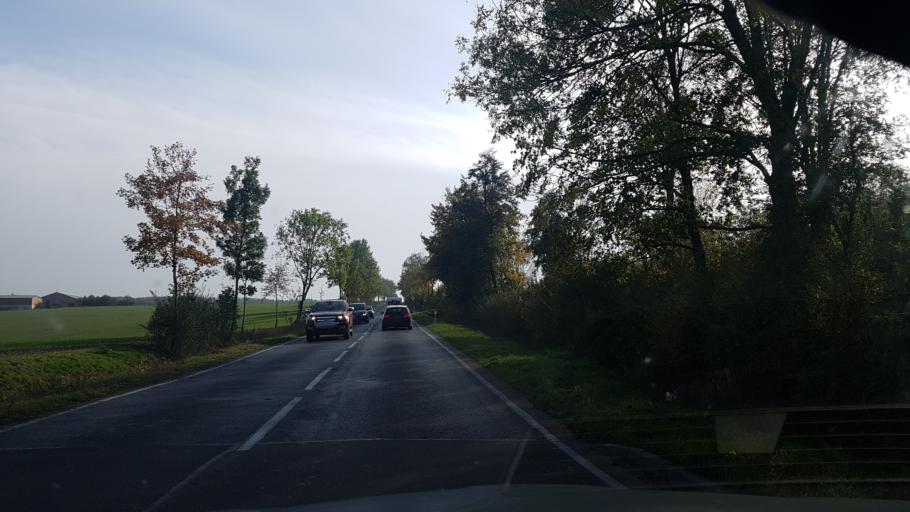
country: DE
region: Saxony
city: Struppen
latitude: 50.9301
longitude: 14.0240
